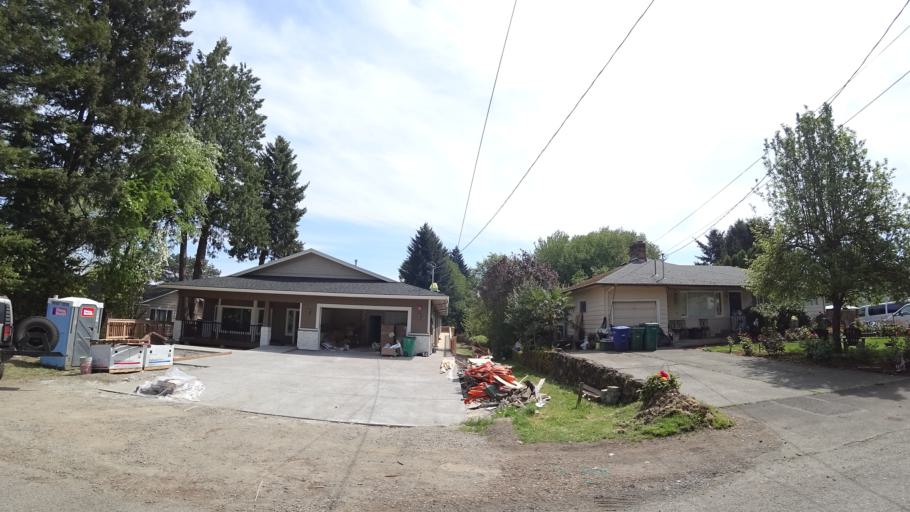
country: US
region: Oregon
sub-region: Clackamas County
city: Oatfield
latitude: 45.4458
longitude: -122.6017
